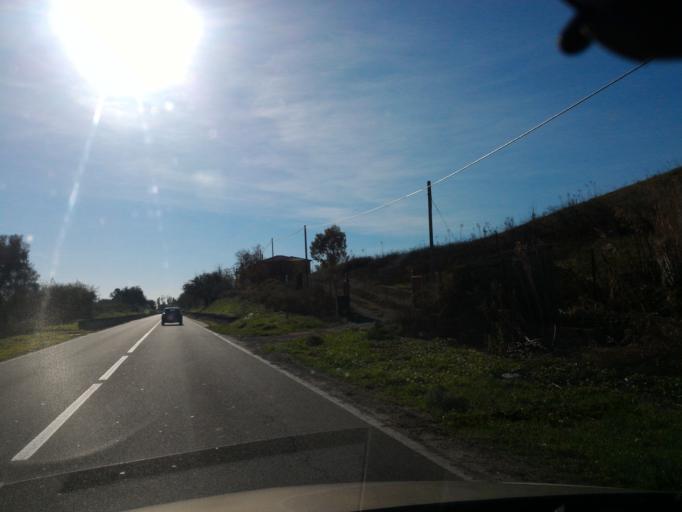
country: IT
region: Calabria
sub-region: Provincia di Crotone
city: Tronca
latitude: 39.2141
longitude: 17.1076
